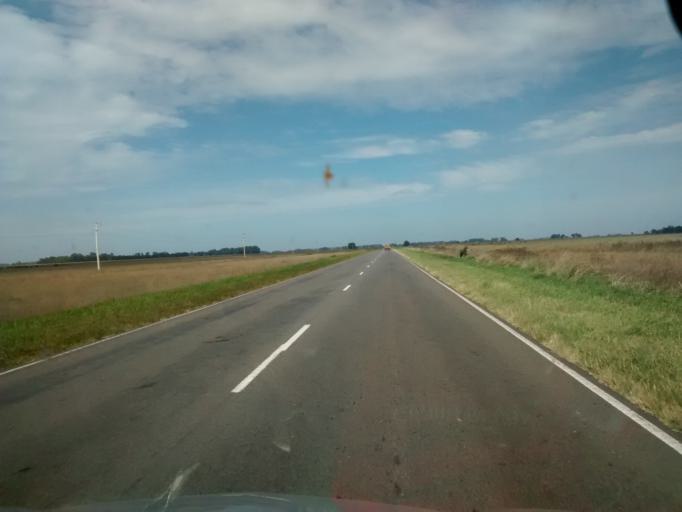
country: AR
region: Buenos Aires
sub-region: Partido de Ayacucho
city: Ayacucho
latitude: -37.0717
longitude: -58.5445
